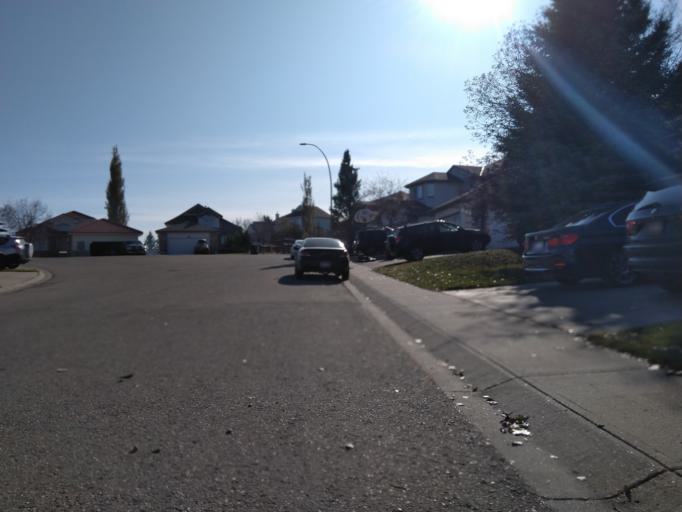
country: CA
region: Alberta
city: Calgary
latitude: 51.1490
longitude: -114.1153
